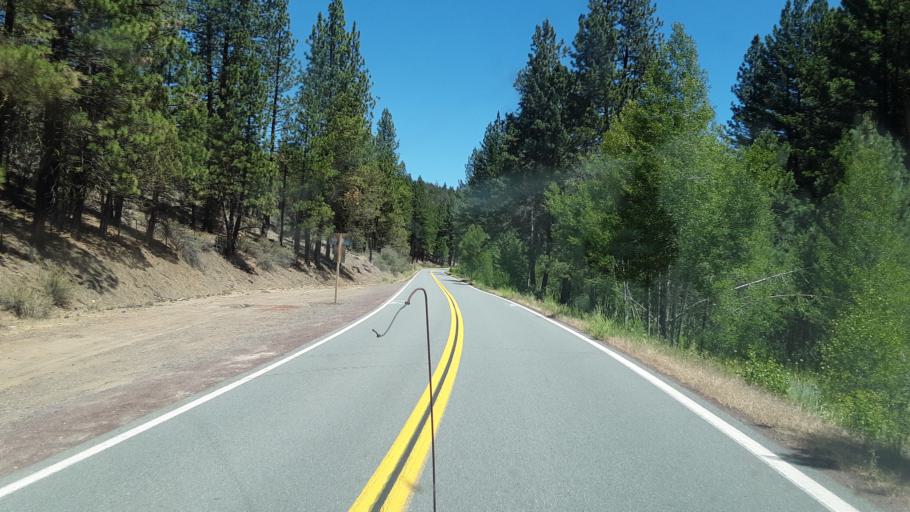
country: US
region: California
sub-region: Modoc County
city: Alturas
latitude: 41.0176
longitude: -120.8464
